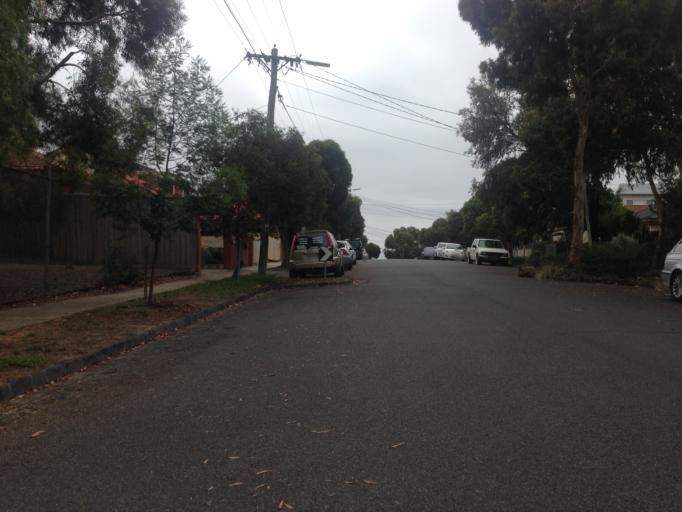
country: AU
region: Victoria
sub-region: Darebin
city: Thornbury
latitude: -37.7611
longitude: 145.0075
